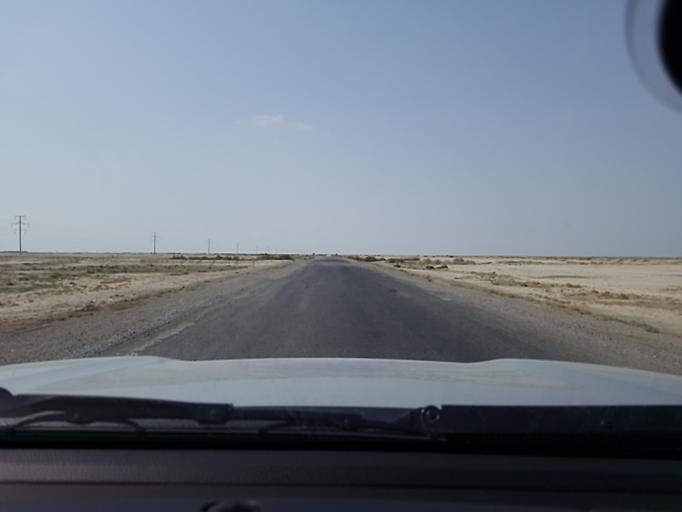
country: TM
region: Balkan
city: Gumdag
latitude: 38.9128
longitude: 54.5915
